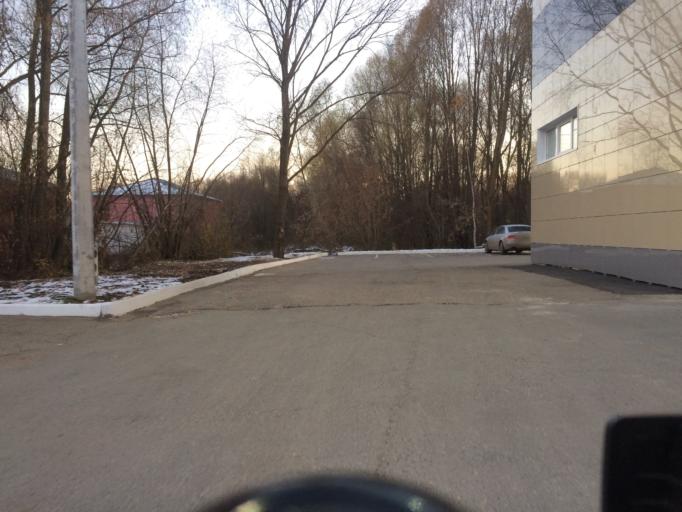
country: RU
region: Mariy-El
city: Yoshkar-Ola
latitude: 56.6260
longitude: 47.9145
